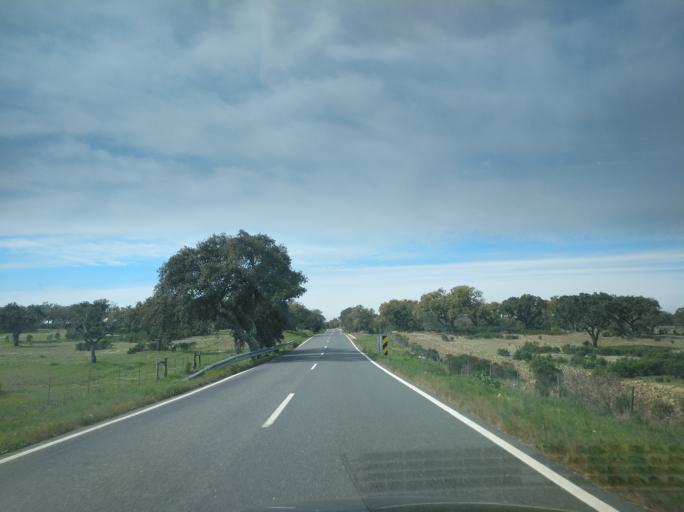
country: PT
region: Beja
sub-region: Mertola
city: Mertola
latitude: 37.7389
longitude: -7.7801
